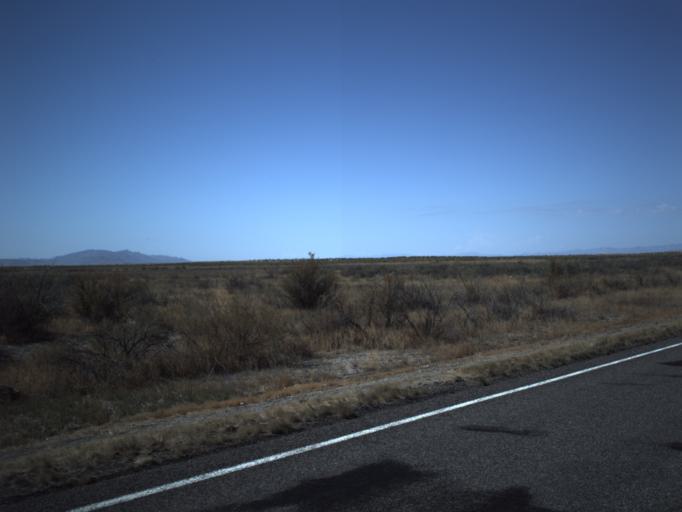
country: US
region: Utah
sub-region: Millard County
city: Delta
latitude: 39.3120
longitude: -112.7672
